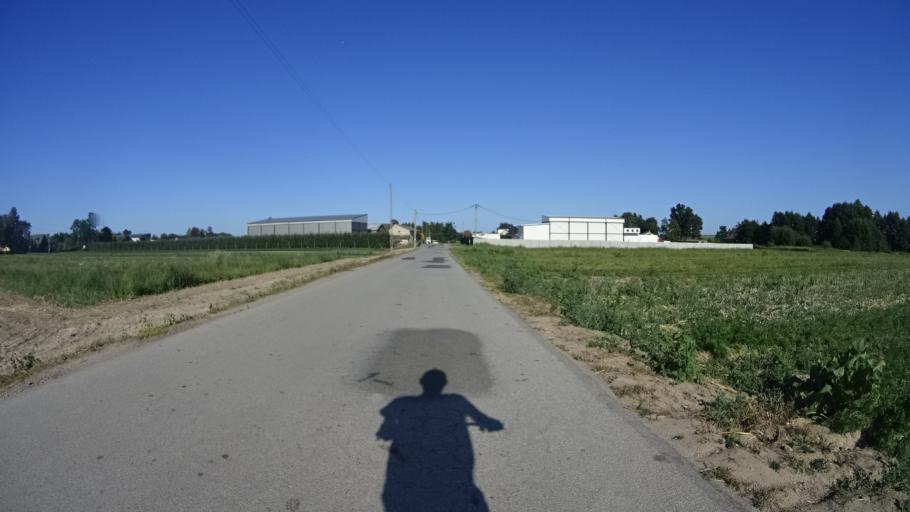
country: PL
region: Masovian Voivodeship
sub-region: Powiat bialobrzeski
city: Wysmierzyce
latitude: 51.6726
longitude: 20.8273
